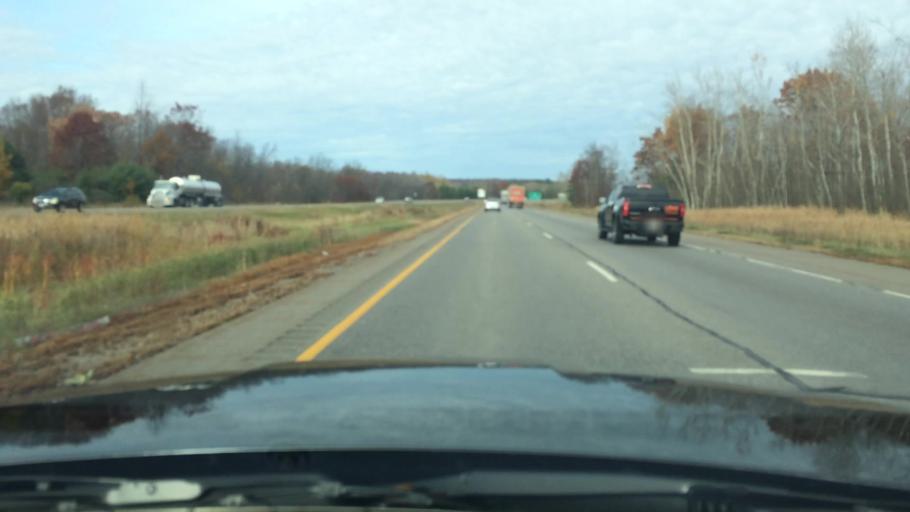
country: US
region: Wisconsin
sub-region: Marathon County
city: Mosinee
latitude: 44.7999
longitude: -89.6786
